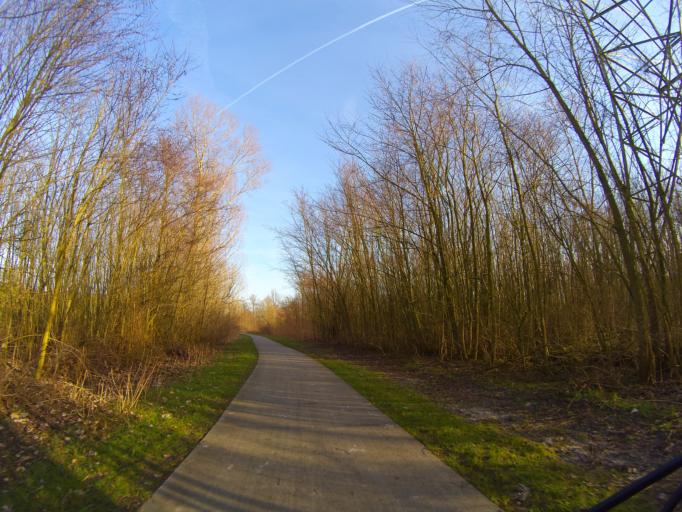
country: NL
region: Utrecht
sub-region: Gemeente Bunschoten
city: Bunschoten
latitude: 52.2548
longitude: 5.4011
